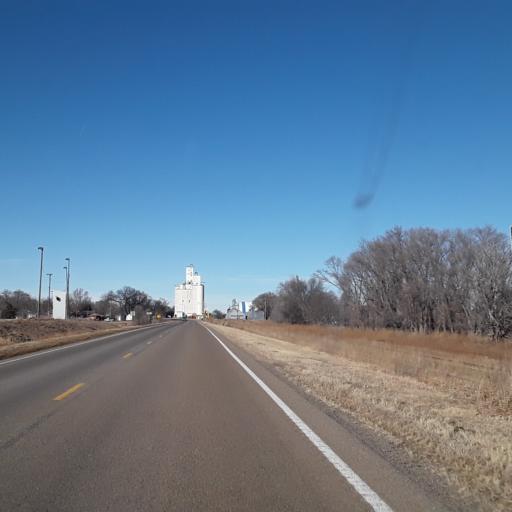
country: US
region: Nebraska
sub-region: Frontier County
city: Stockville
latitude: 40.6534
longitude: -100.6159
